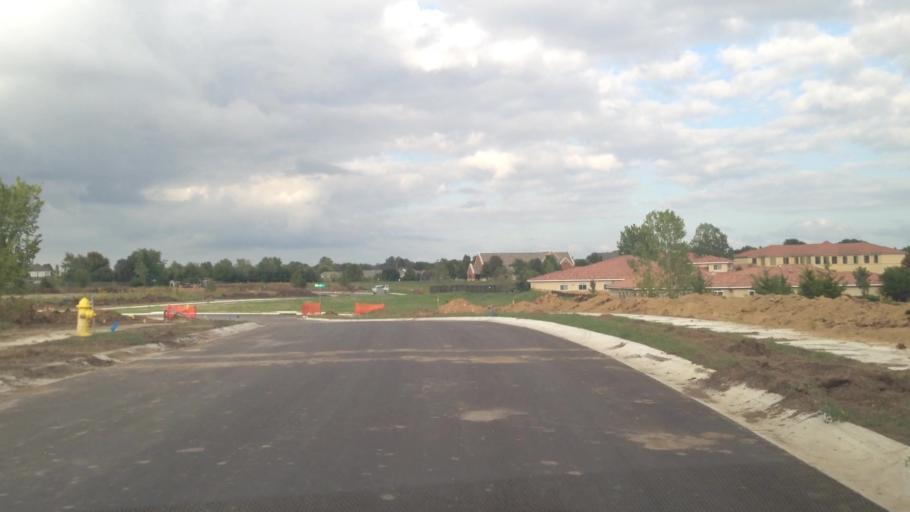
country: US
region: Kansas
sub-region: Douglas County
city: Lawrence
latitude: 38.9644
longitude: -95.3114
